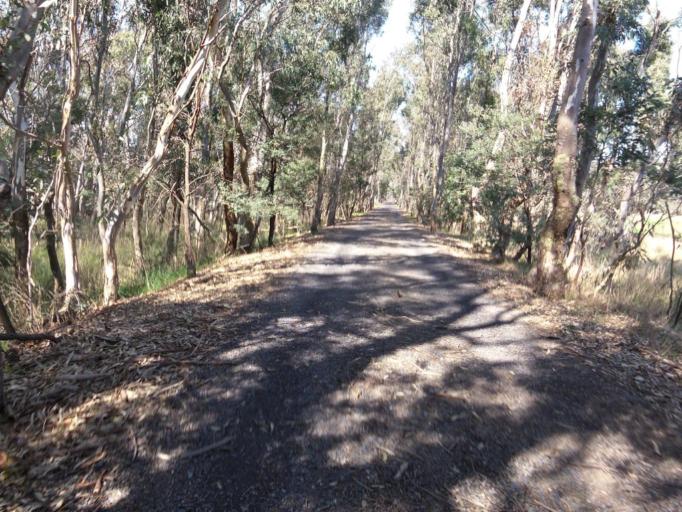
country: AU
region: Victoria
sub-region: Murrindindi
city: Alexandra
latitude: -36.9839
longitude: 145.7275
